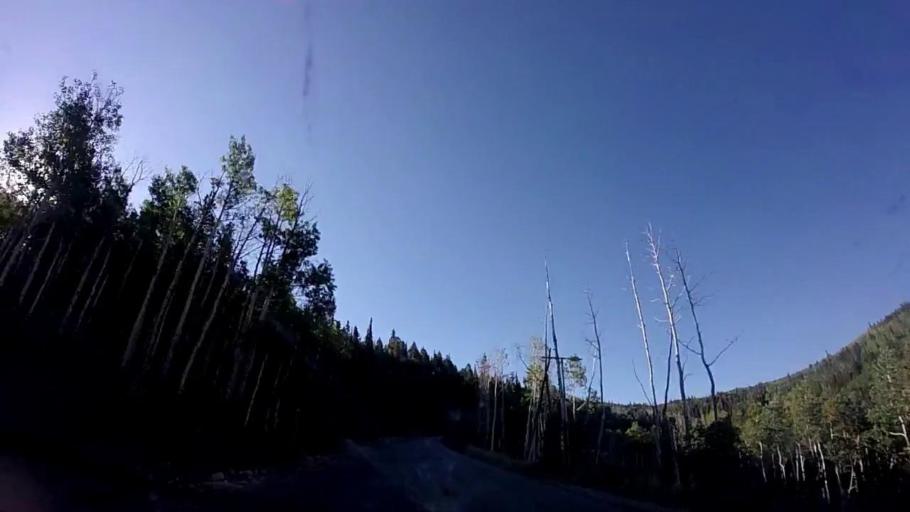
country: US
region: Utah
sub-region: Summit County
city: Park City
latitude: 40.6152
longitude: -111.5073
